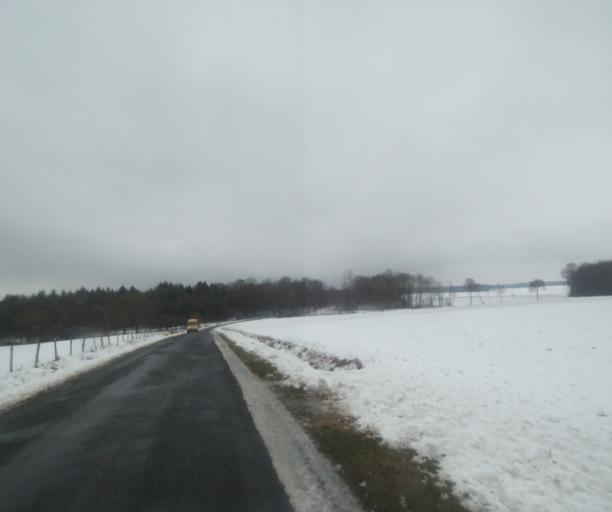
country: FR
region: Champagne-Ardenne
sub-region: Departement de la Haute-Marne
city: Montier-en-Der
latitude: 48.4690
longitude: 4.8125
